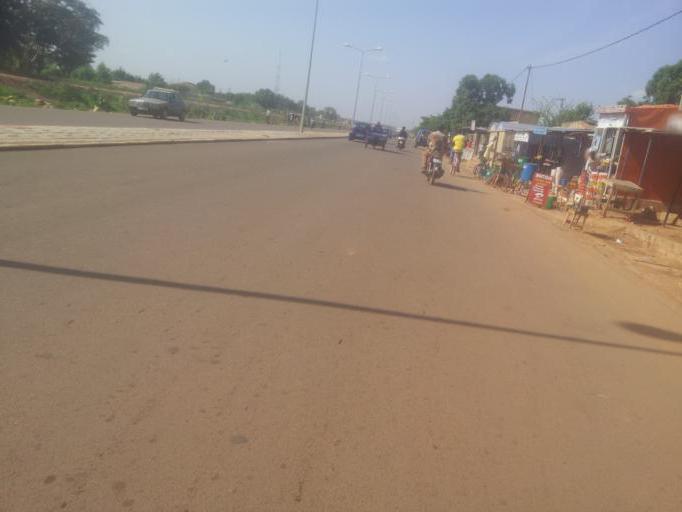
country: BF
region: Centre
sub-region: Kadiogo Province
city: Ouagadougou
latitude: 12.3785
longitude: -1.5700
